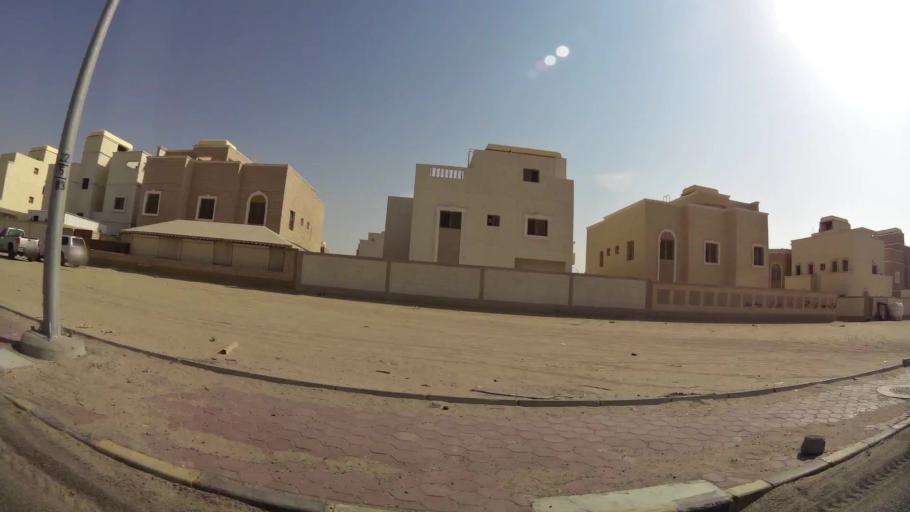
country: KW
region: Al Ahmadi
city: Al Wafrah
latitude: 28.7897
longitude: 48.0674
